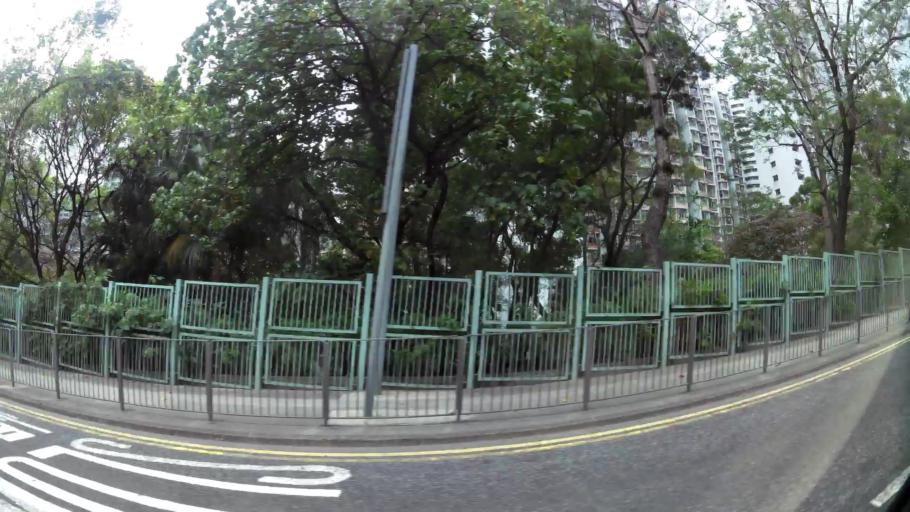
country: HK
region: Wong Tai Sin
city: Wong Tai Sin
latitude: 22.3424
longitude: 114.1870
